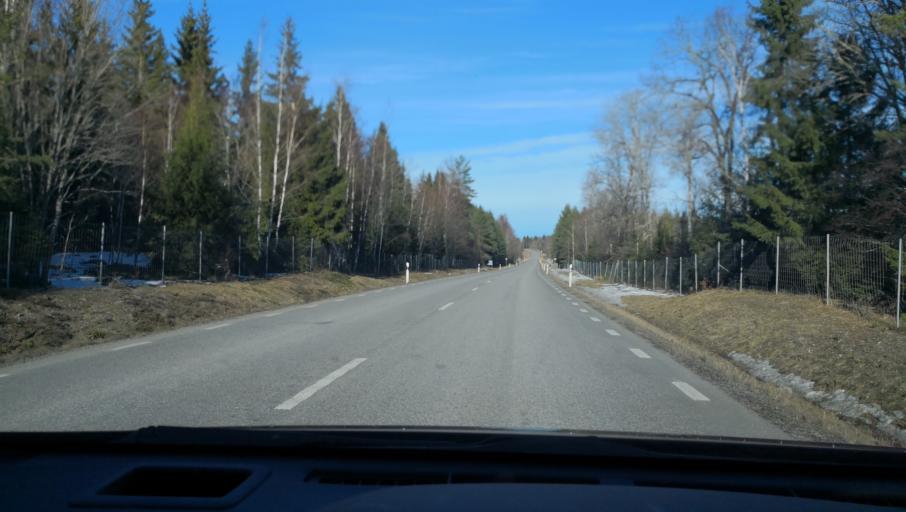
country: SE
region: Uppsala
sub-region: Uppsala Kommun
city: Vattholma
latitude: 60.0542
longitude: 17.7524
